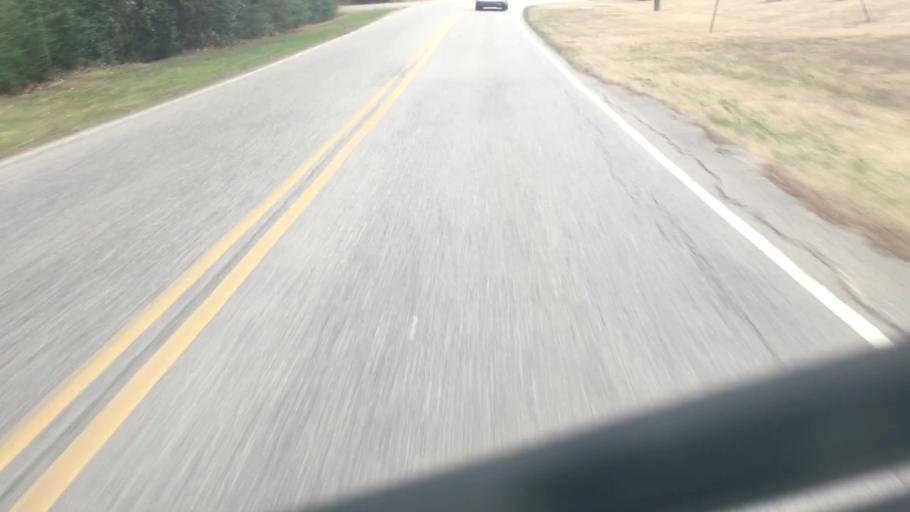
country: US
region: Alabama
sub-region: Jefferson County
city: Hoover
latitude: 33.3566
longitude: -86.8080
